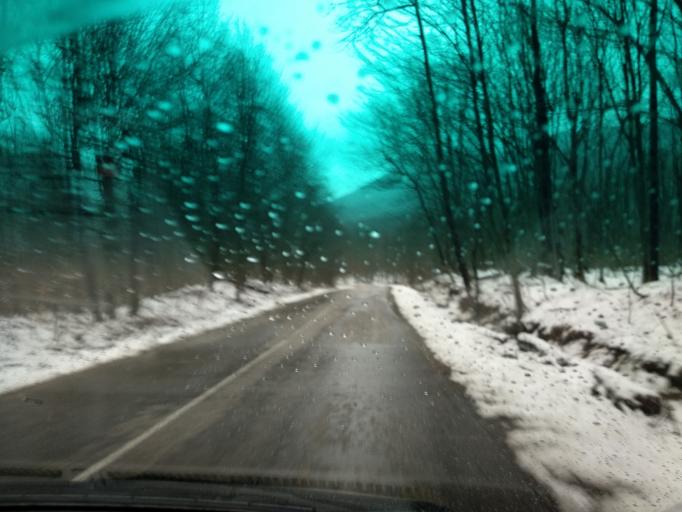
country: RU
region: Krasnodarskiy
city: Khadyzhensk
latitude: 44.2156
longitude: 39.4005
